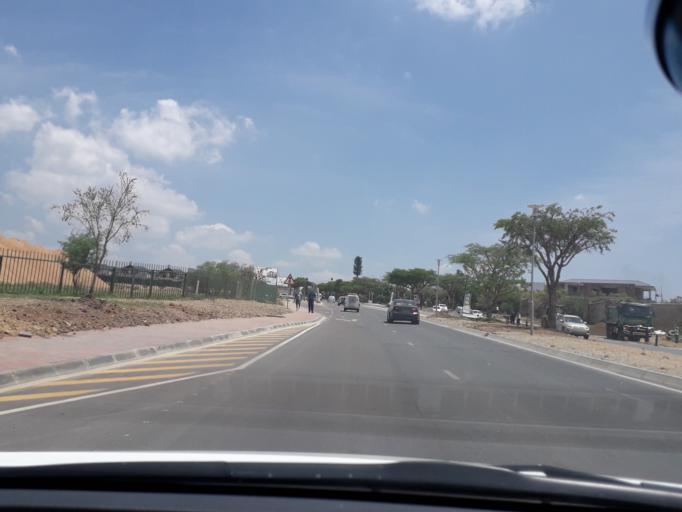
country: ZA
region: Gauteng
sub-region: City of Johannesburg Metropolitan Municipality
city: Midrand
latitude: -26.0223
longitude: 28.0869
